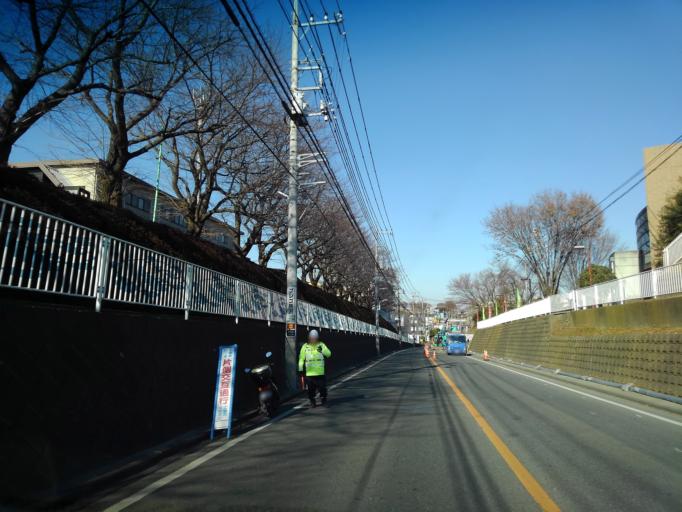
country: JP
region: Saitama
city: Oi
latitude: 35.8031
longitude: 139.5222
